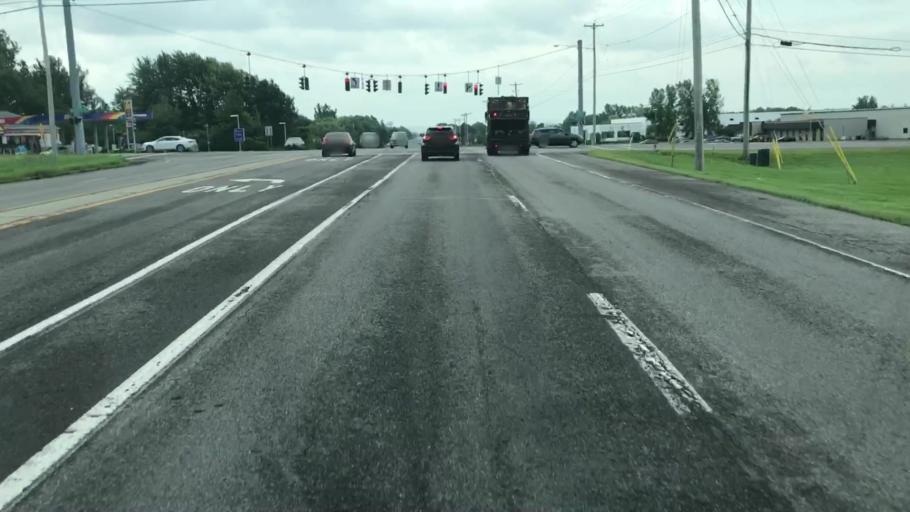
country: US
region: New York
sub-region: Onondaga County
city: Liverpool
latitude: 43.1425
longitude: -76.1877
